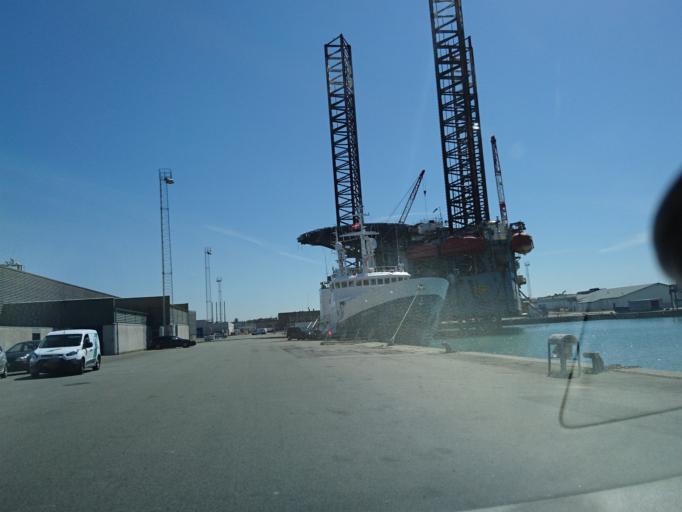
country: DK
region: North Denmark
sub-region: Hjorring Kommune
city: Hirtshals
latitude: 57.5929
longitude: 9.9744
